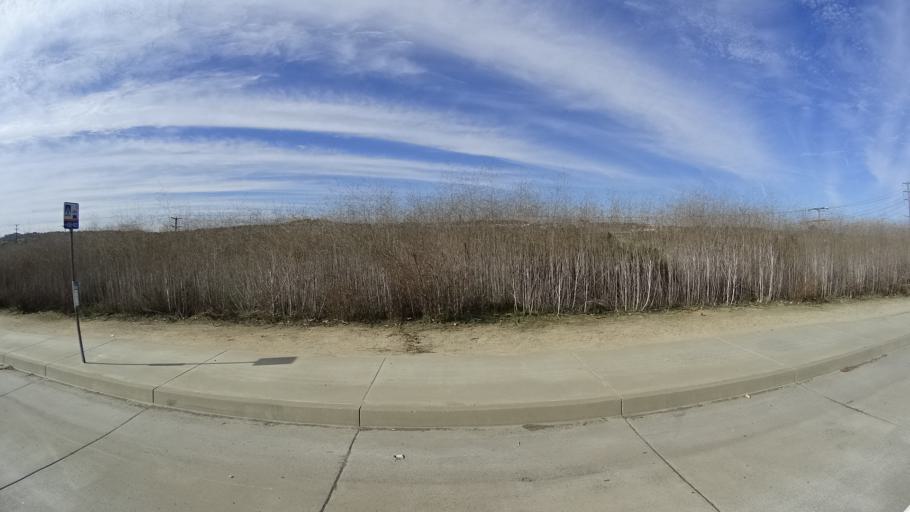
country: US
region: California
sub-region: Orange County
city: Aliso Viejo
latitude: 33.5746
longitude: -117.7124
